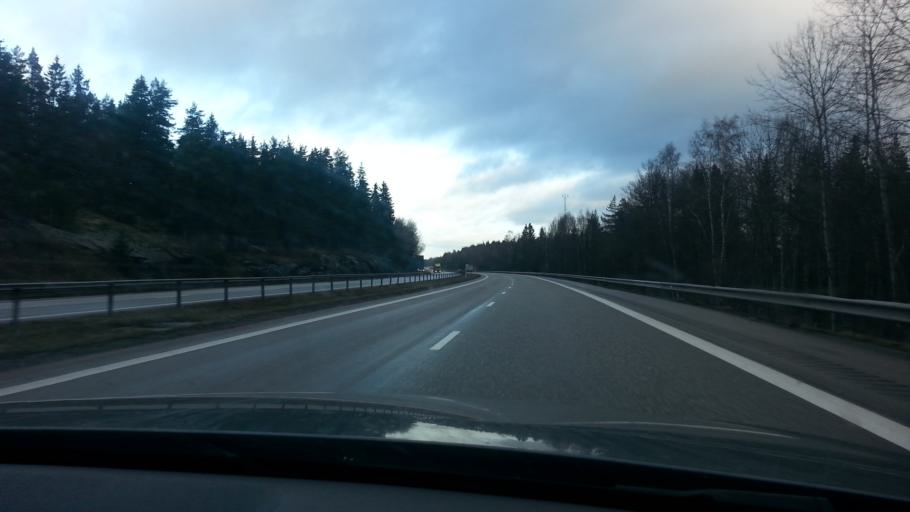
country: SE
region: OEstergoetland
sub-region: Odeshogs Kommun
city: OEdeshoeg
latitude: 58.1562
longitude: 14.5800
